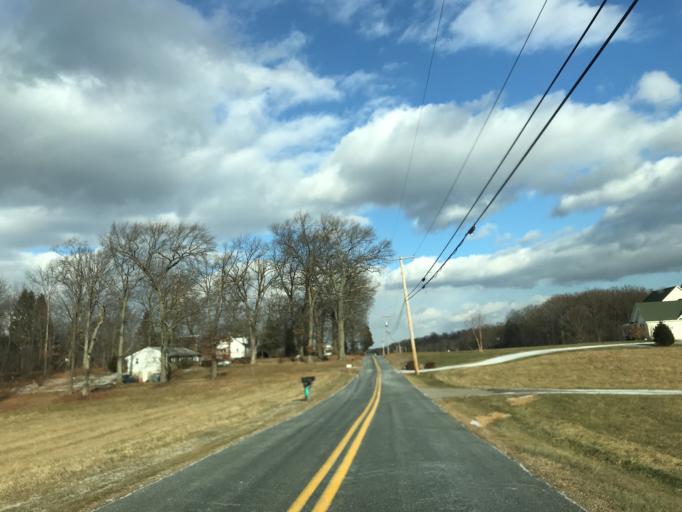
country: US
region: Maryland
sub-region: Harford County
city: Jarrettsville
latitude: 39.6152
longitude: -76.4399
